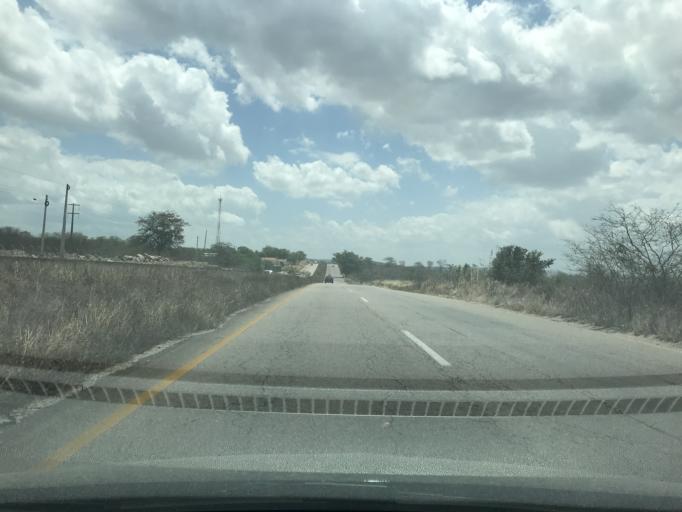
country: BR
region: Pernambuco
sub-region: Caruaru
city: Caruaru
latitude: -8.2974
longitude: -35.8975
